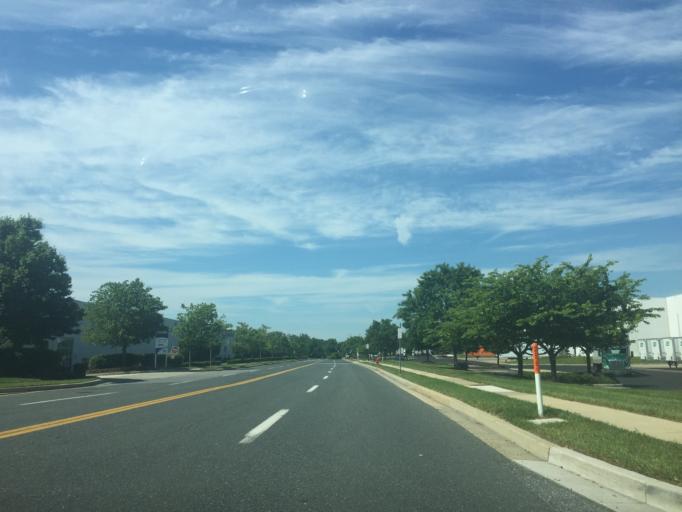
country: US
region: Maryland
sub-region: Baltimore County
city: Rossville
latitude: 39.3268
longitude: -76.4867
